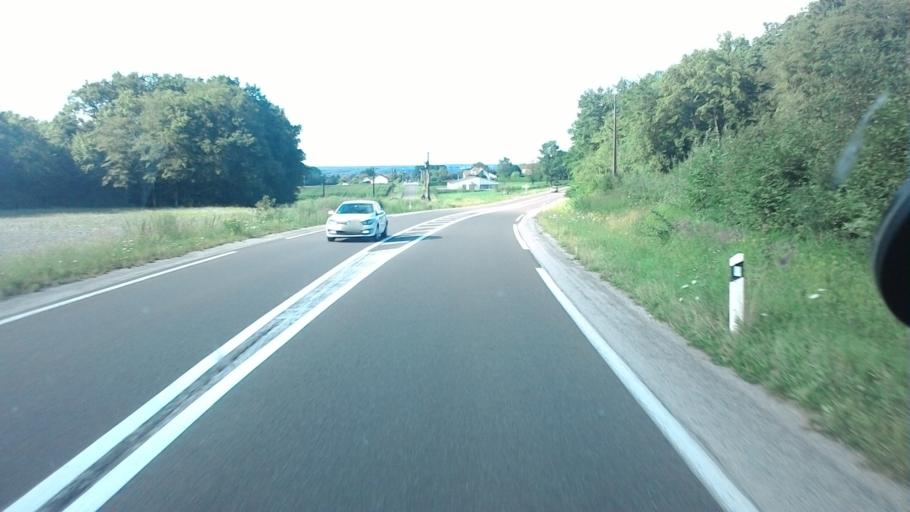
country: FR
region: Franche-Comte
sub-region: Departement de la Haute-Saone
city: Luxeuil-les-Bains
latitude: 47.7657
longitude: 6.3412
